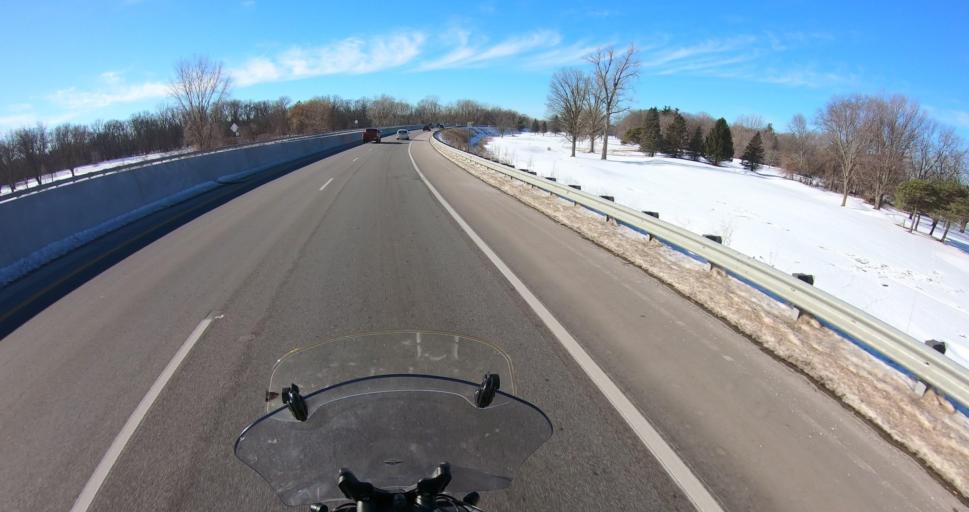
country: US
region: Michigan
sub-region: Midland County
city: Midland
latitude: 43.6132
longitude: -84.2499
